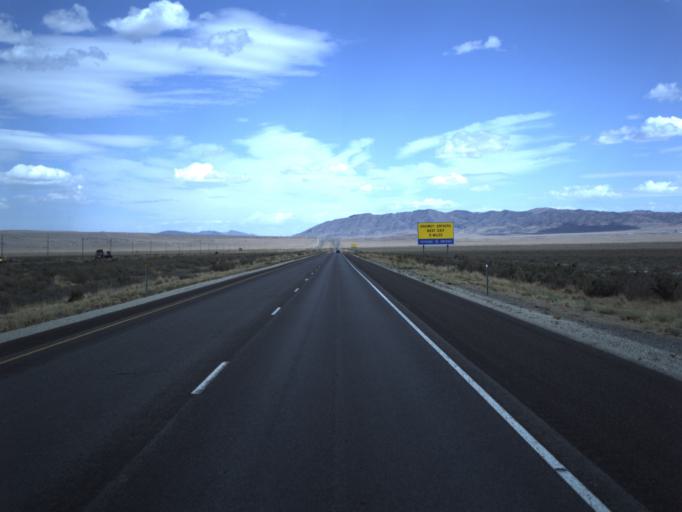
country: US
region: Utah
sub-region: Tooele County
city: Grantsville
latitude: 40.7353
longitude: -113.0999
